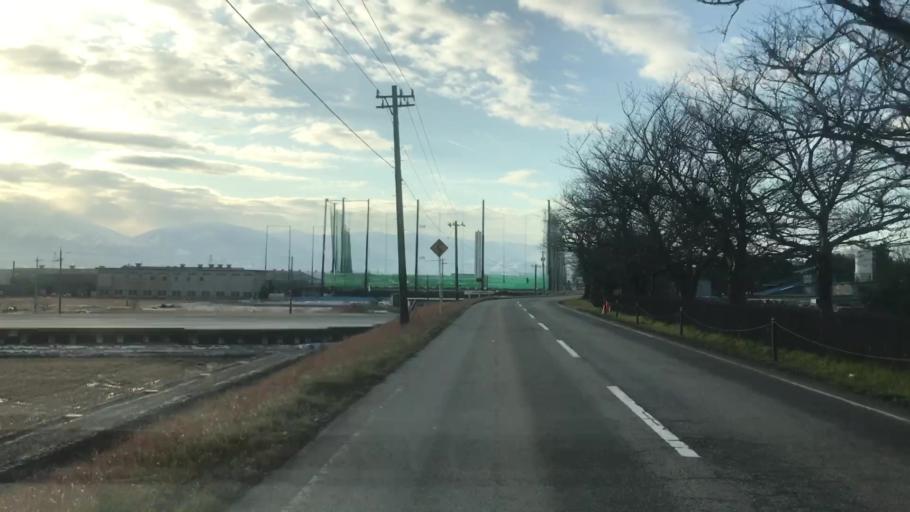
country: JP
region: Toyama
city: Toyama-shi
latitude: 36.6985
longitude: 137.2821
